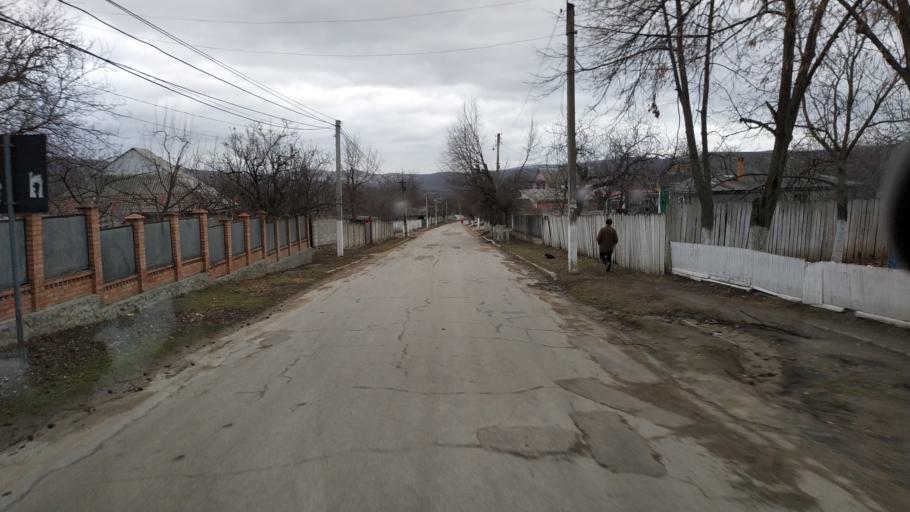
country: MD
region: Calarasi
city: Calarasi
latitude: 47.2622
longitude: 28.1341
